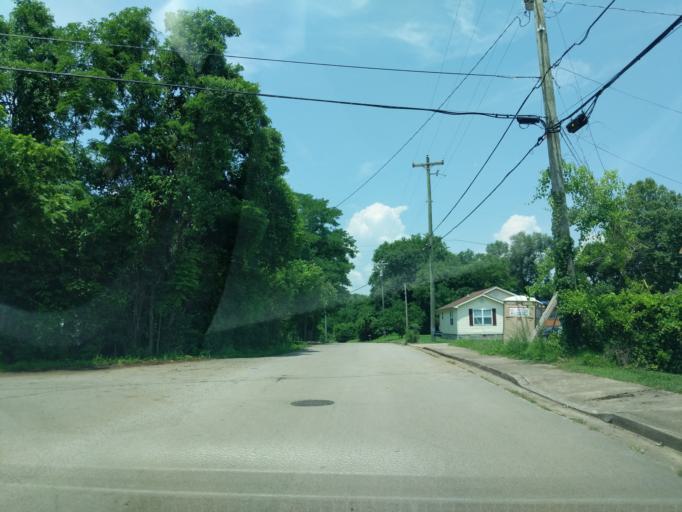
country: US
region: Tennessee
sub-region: Davidson County
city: Lakewood
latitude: 36.2269
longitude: -86.6276
